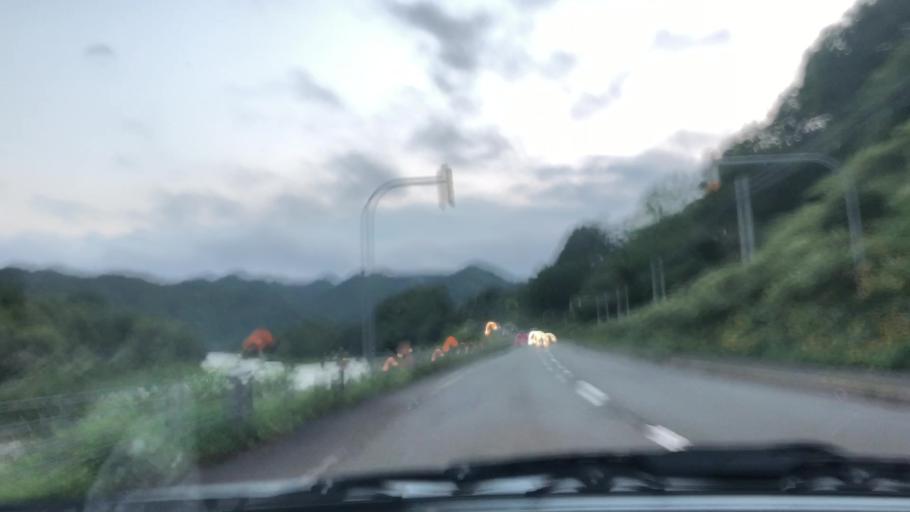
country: JP
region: Hokkaido
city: Chitose
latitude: 42.9069
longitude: 142.0122
